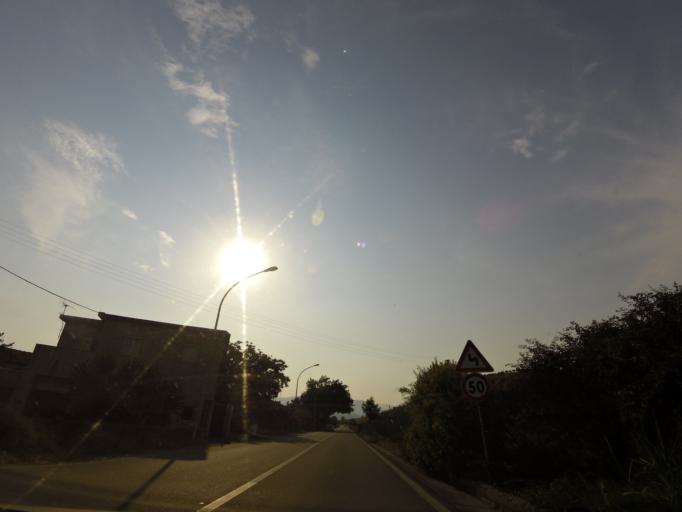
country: IT
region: Calabria
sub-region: Provincia di Reggio Calabria
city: Monasterace
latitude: 38.4382
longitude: 16.5528
